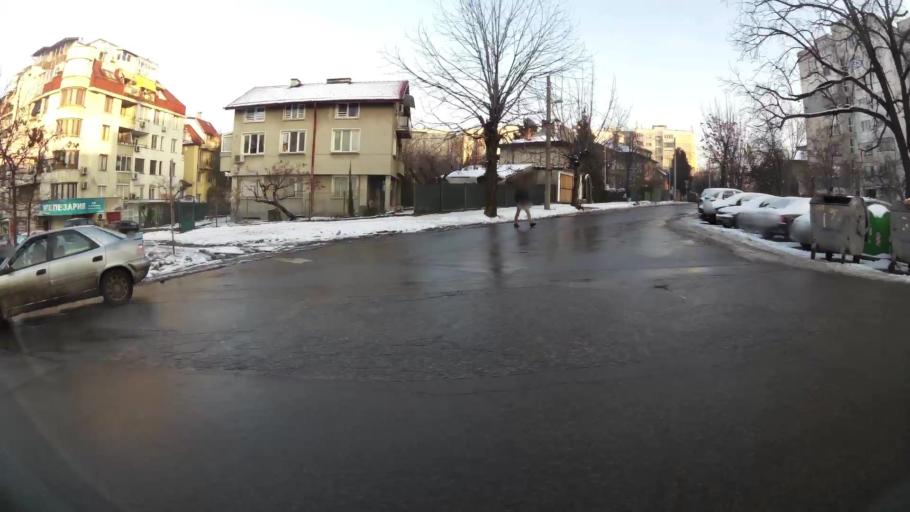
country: BG
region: Sofia-Capital
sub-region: Stolichna Obshtina
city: Sofia
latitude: 42.6943
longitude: 23.3602
